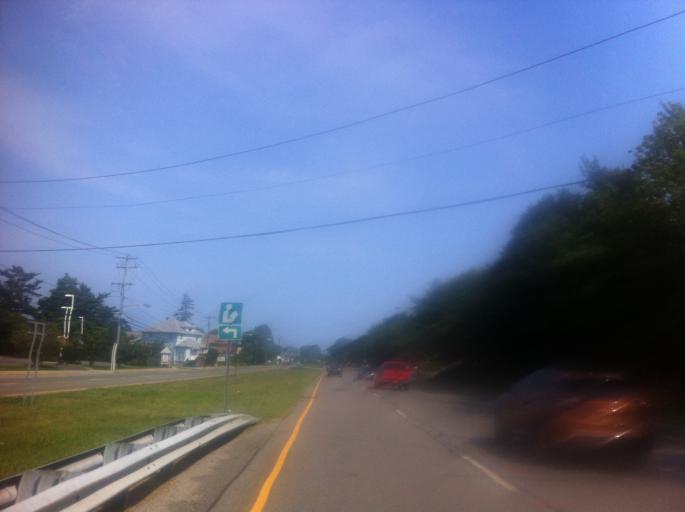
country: US
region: New York
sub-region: Suffolk County
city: West Babylon
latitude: 40.7088
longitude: -73.3557
